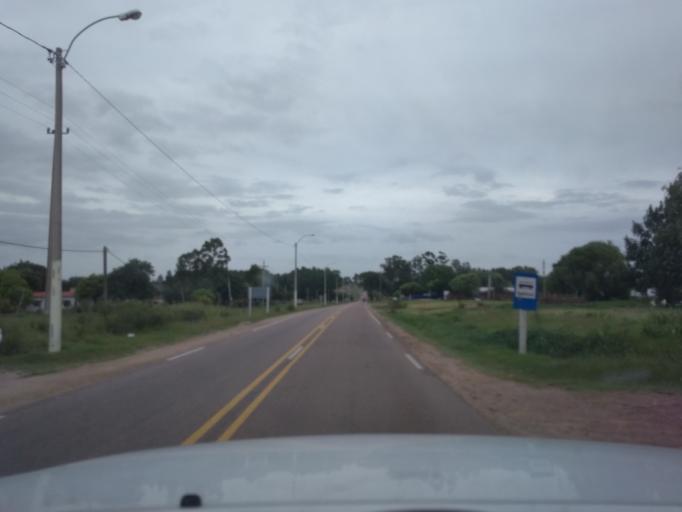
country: UY
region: Canelones
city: Tala
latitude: -34.3520
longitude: -55.7688
